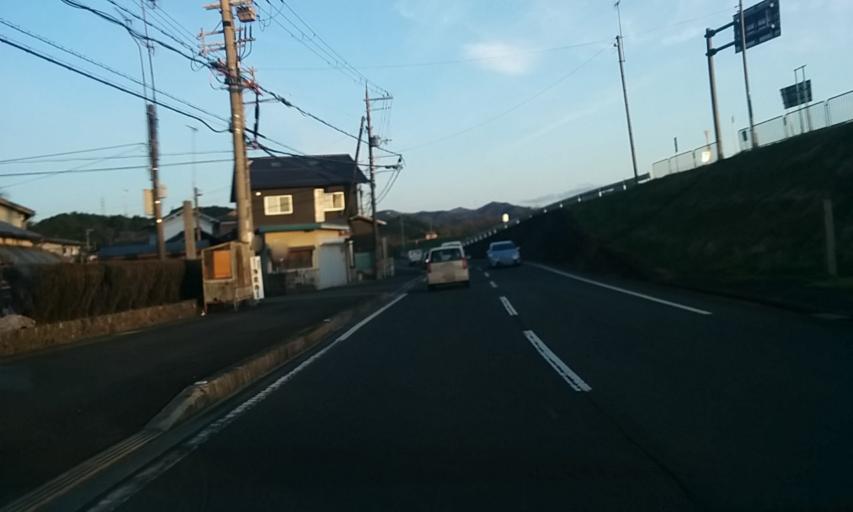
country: JP
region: Kyoto
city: Ayabe
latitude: 35.3135
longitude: 135.2466
